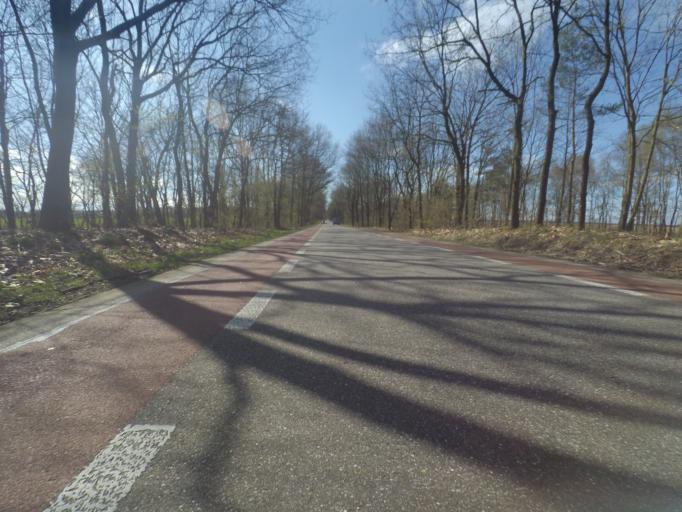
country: NL
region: Gelderland
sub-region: Gemeente Arnhem
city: Hoogkamp
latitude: 52.1002
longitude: 5.8789
